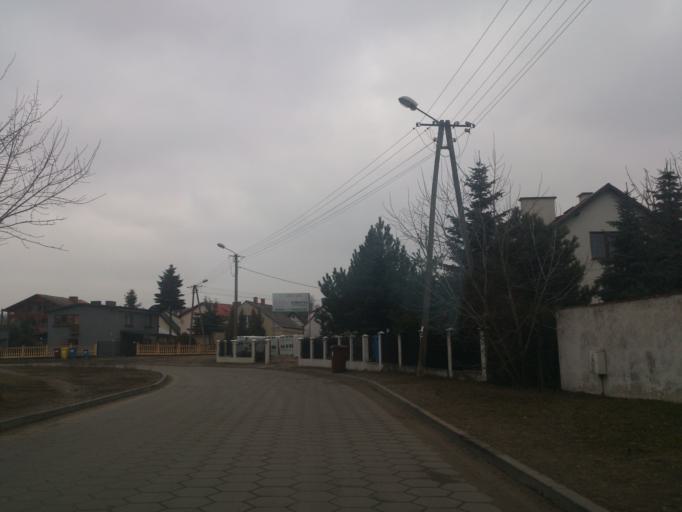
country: PL
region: Kujawsko-Pomorskie
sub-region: Powiat golubsko-dobrzynski
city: Golub-Dobrzyn
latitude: 53.1096
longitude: 19.0509
